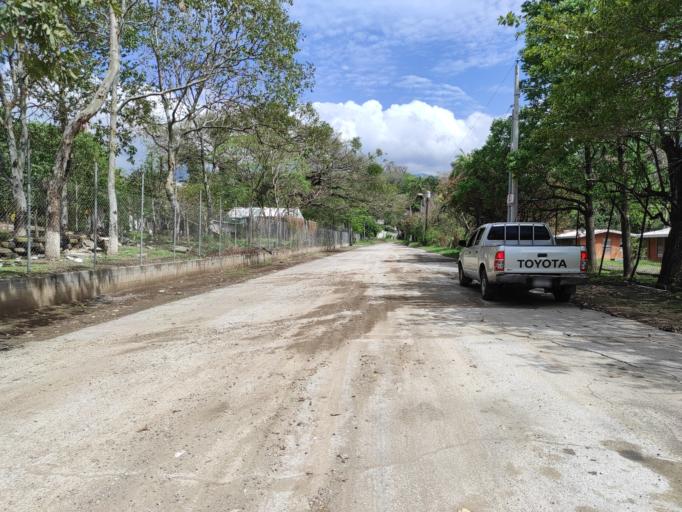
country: GT
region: Guatemala
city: Amatitlan
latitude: 14.4819
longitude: -90.6088
